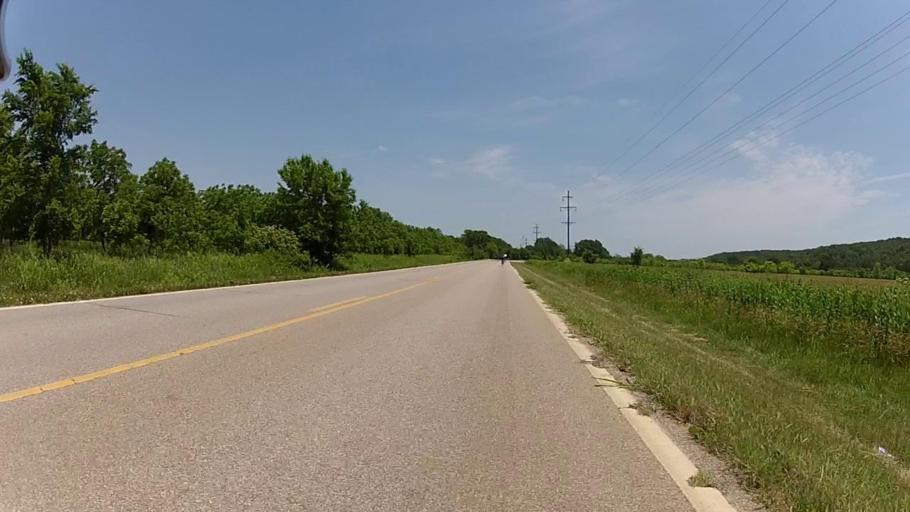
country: US
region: Kansas
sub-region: Chautauqua County
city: Sedan
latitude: 37.1201
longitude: -96.2258
